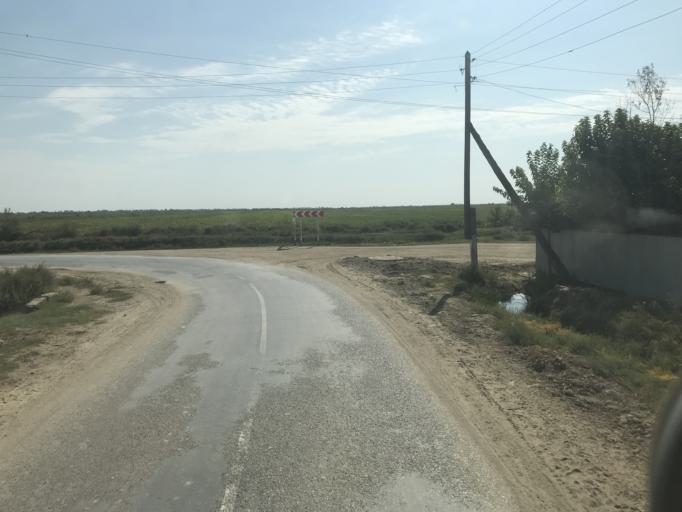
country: KZ
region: Ongtustik Qazaqstan
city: Myrzakent
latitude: 40.6640
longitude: 68.6327
